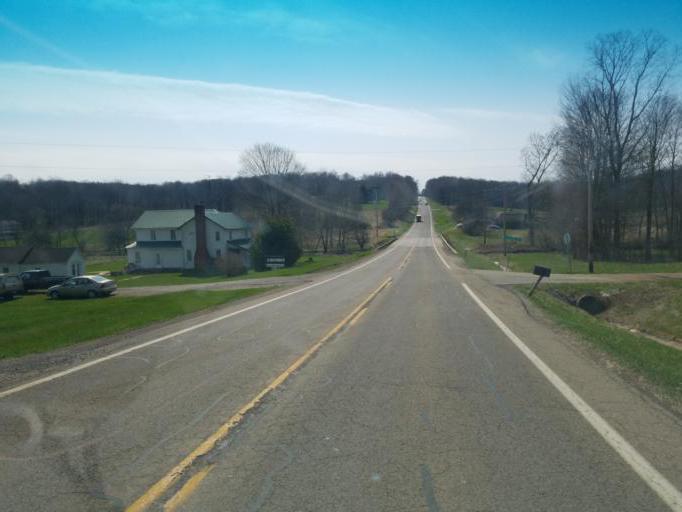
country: US
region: Ohio
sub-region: Knox County
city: Gambier
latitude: 40.4595
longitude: -82.4027
